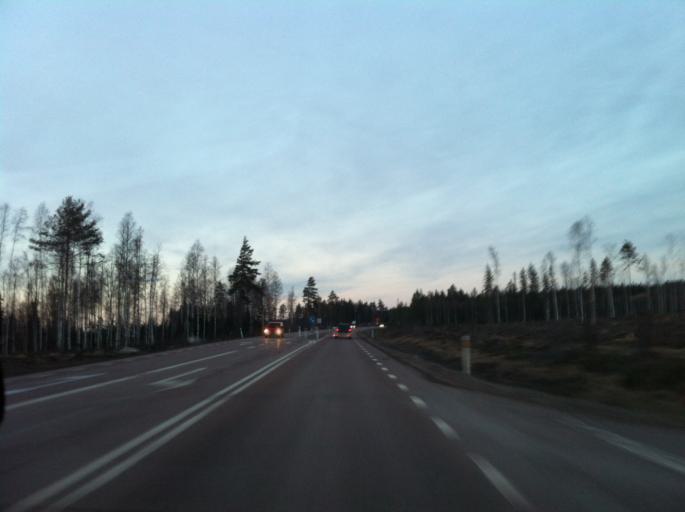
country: SE
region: Dalarna
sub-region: Mora Kommun
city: Mora
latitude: 61.0387
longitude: 14.5977
